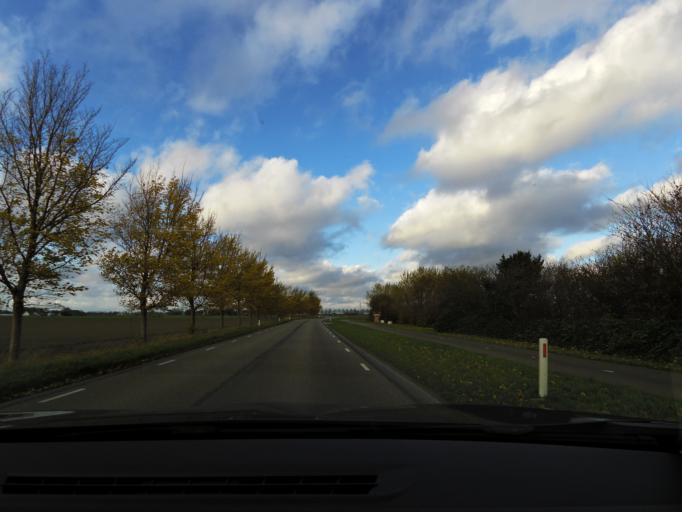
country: NL
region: South Holland
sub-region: Gemeente Goeree-Overflakkee
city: Middelharnis
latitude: 51.7055
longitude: 4.2637
